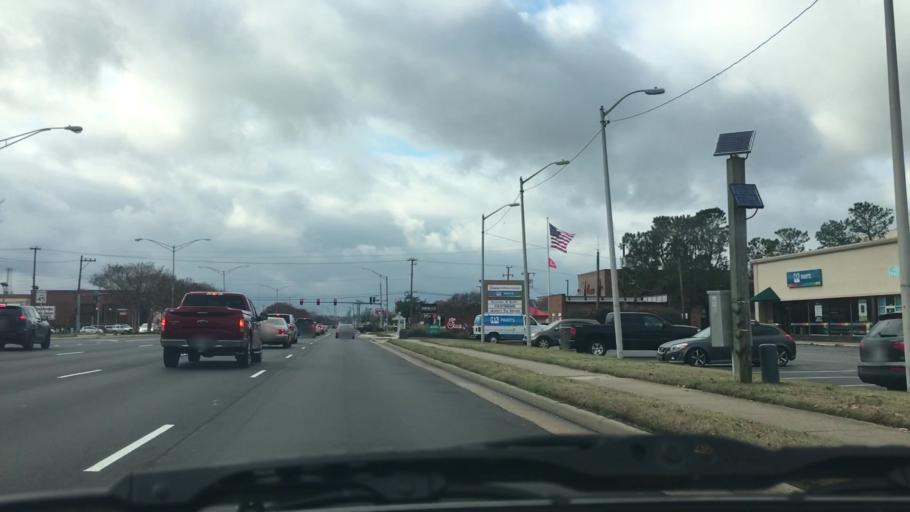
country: US
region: Virginia
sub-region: City of Chesapeake
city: Chesapeake
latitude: 36.8438
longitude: -76.1400
